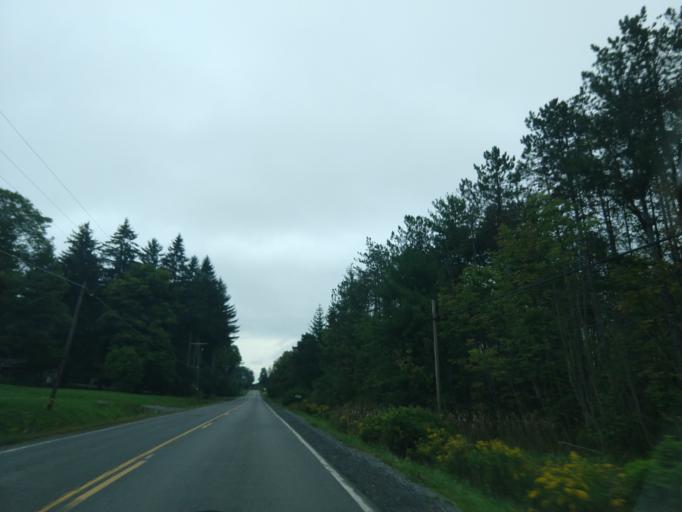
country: US
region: New York
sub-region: Tompkins County
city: South Hill
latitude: 42.4129
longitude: -76.4749
